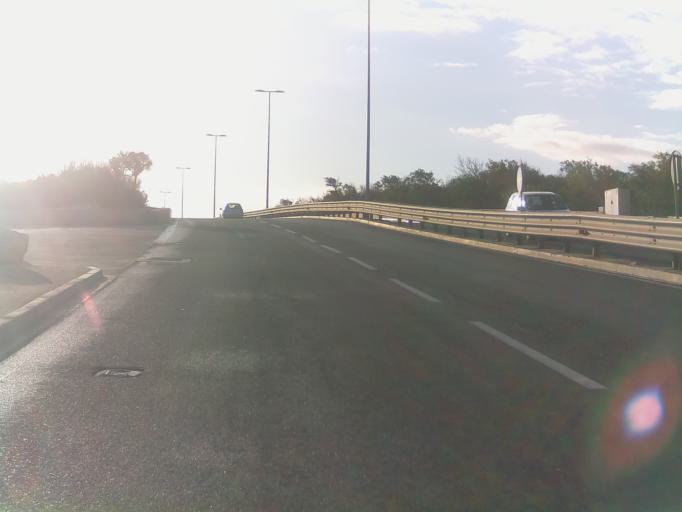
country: MT
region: Il-Mellieha
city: Mellieha
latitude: 35.9802
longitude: 14.3423
